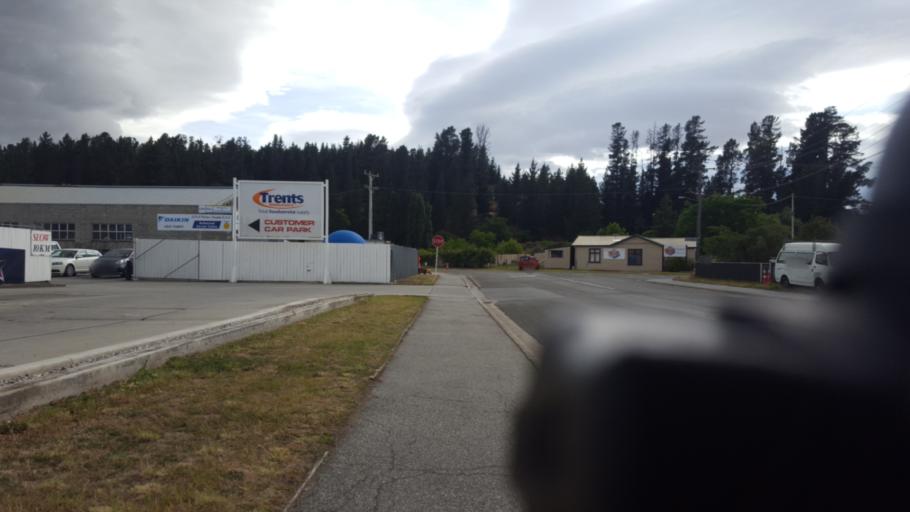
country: NZ
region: Otago
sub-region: Queenstown-Lakes District
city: Wanaka
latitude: -45.2454
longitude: 169.3958
